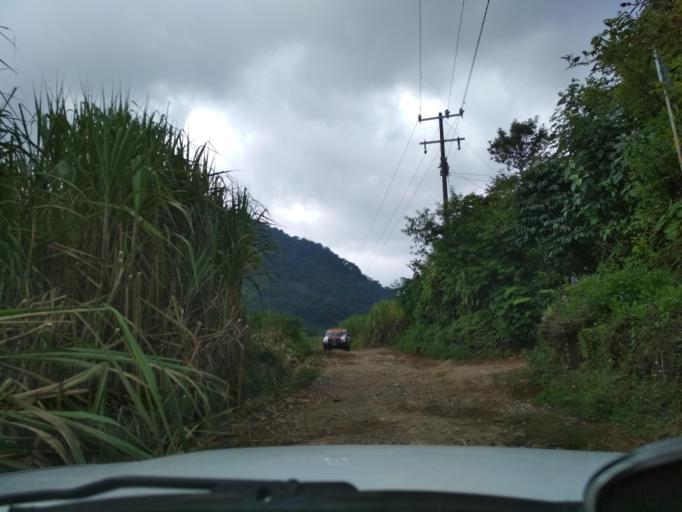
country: MX
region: Veracruz
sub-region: Fortin
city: Santa Lucia Potrerillo
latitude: 18.9503
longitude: -97.0627
